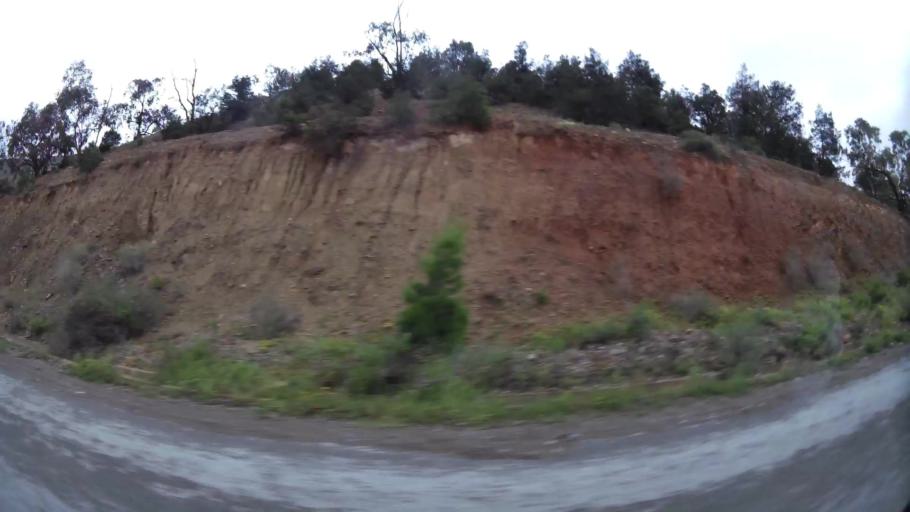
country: MA
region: Taza-Al Hoceima-Taounate
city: Imzourene
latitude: 34.9459
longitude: -3.8074
